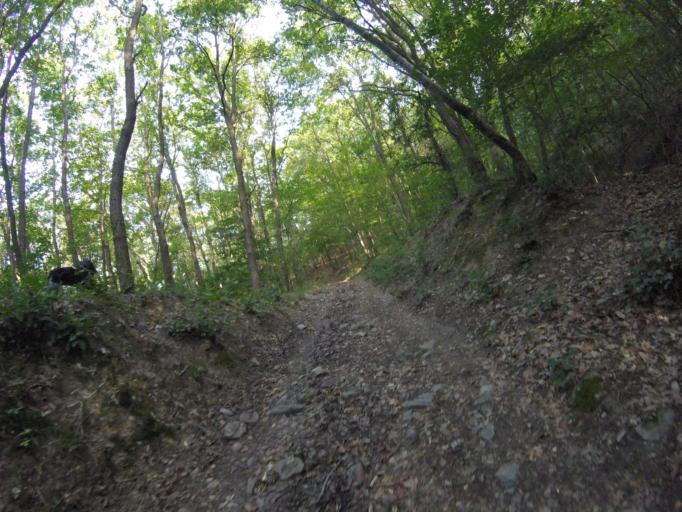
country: HU
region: Pest
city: Pilisszentkereszt
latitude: 47.7017
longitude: 18.9021
